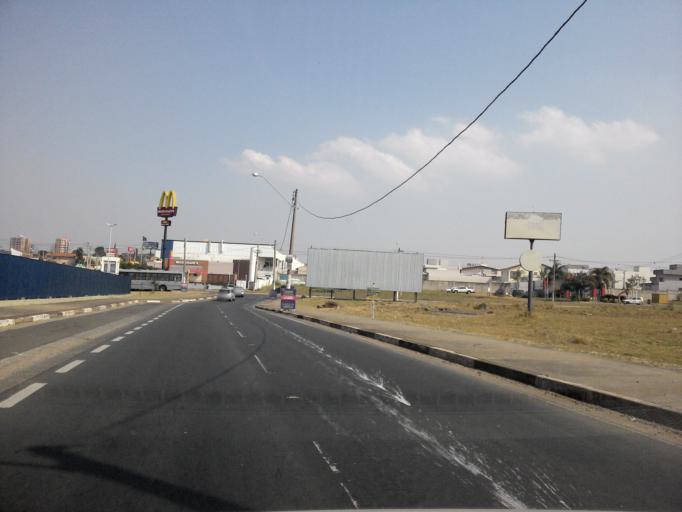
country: BR
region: Sao Paulo
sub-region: Hortolandia
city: Hortolandia
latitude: -22.8665
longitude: -47.2258
